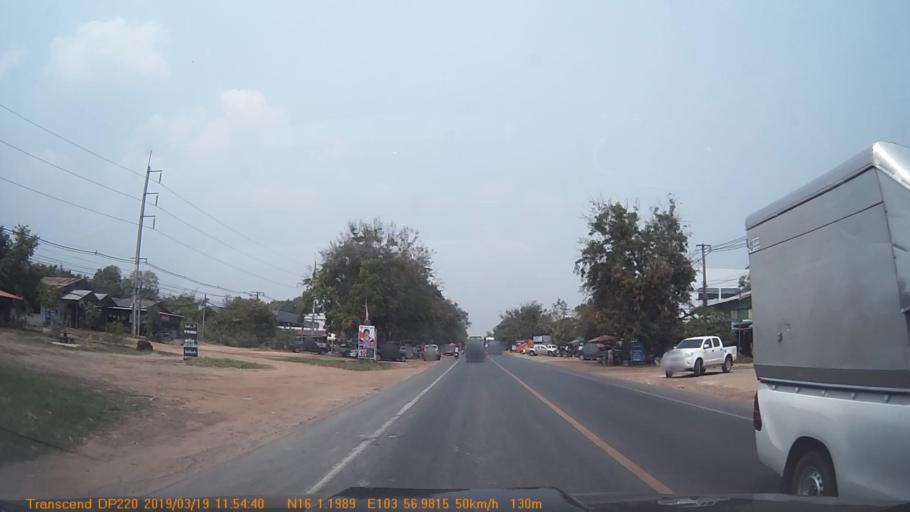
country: TH
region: Roi Et
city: Ban Selaphum
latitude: 16.0201
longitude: 103.9496
